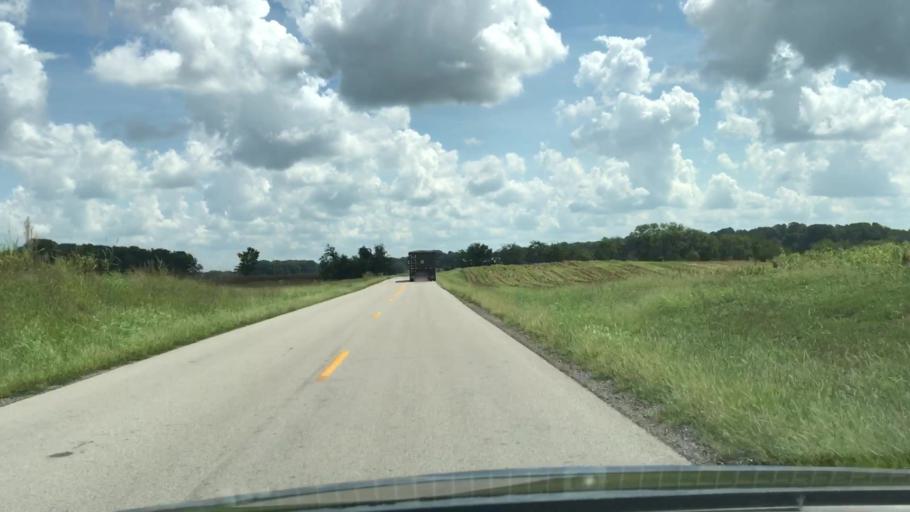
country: US
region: Kentucky
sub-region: Todd County
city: Guthrie
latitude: 36.6498
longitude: -86.9997
